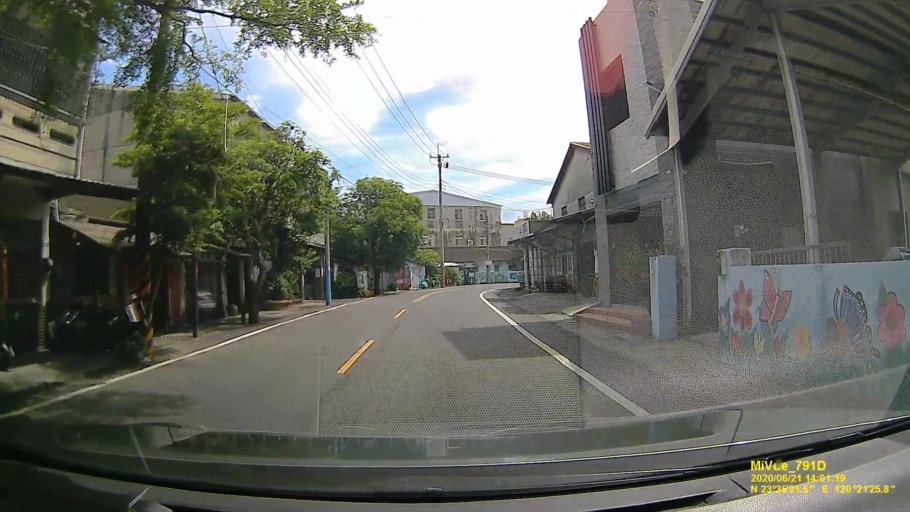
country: TW
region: Taiwan
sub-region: Chiayi
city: Taibao
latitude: 23.5920
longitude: 120.3571
